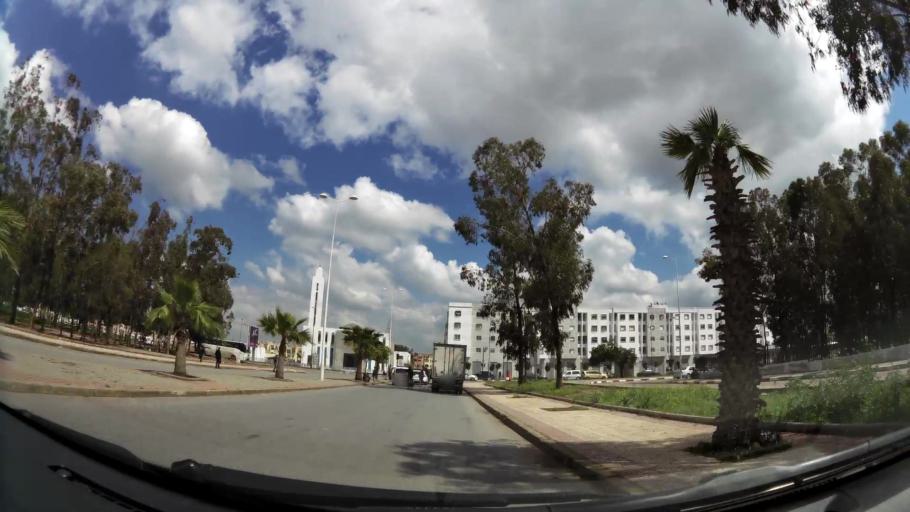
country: MA
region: Chaouia-Ouardigha
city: Nouaseur
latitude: 33.3715
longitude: -7.5432
